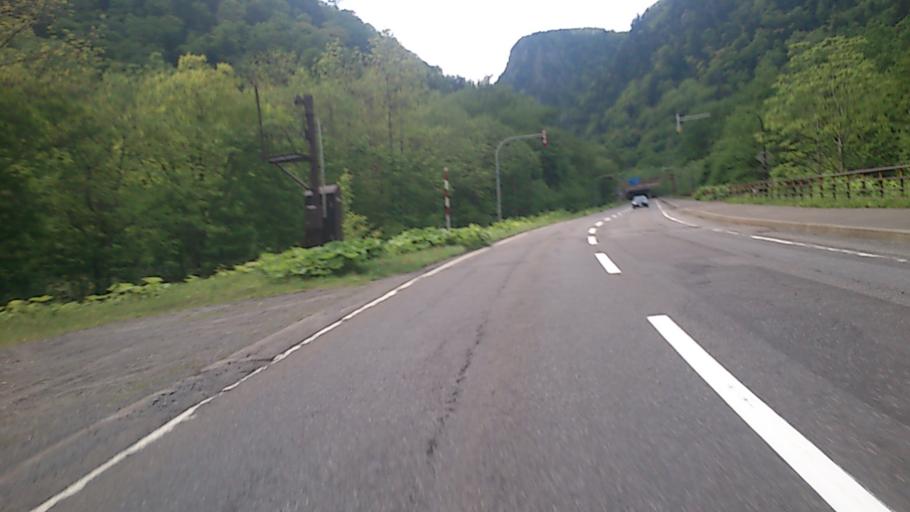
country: JP
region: Hokkaido
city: Kamikawa
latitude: 43.7476
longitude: 142.9344
